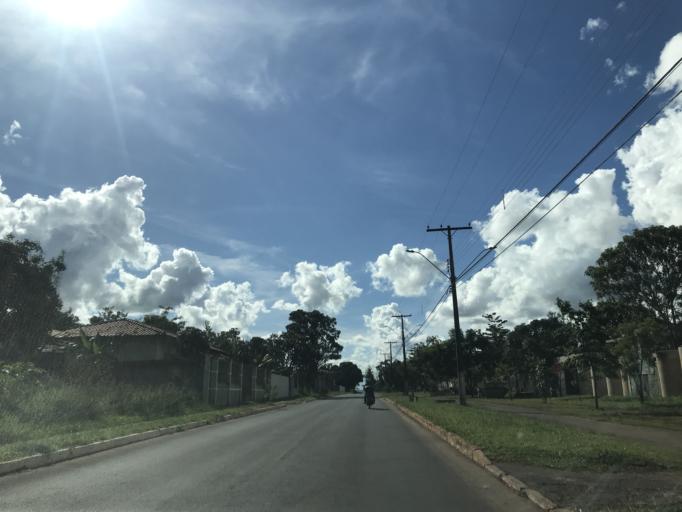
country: BR
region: Federal District
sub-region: Brasilia
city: Brasilia
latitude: -15.7456
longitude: -47.7516
